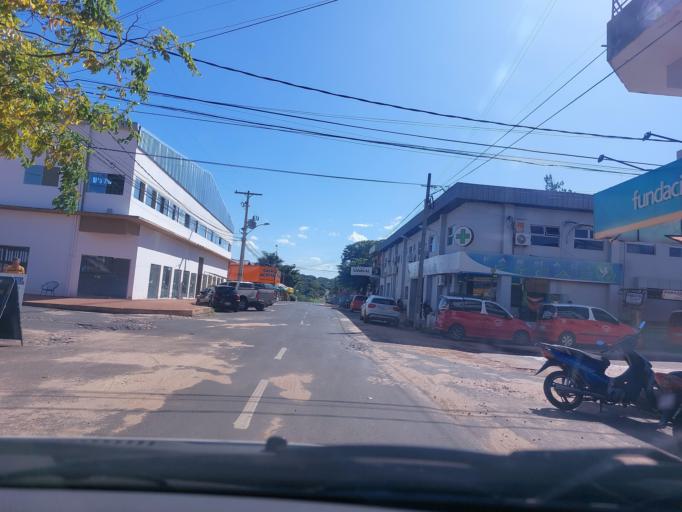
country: PY
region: San Pedro
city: Guayaybi
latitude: -24.6626
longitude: -56.4441
